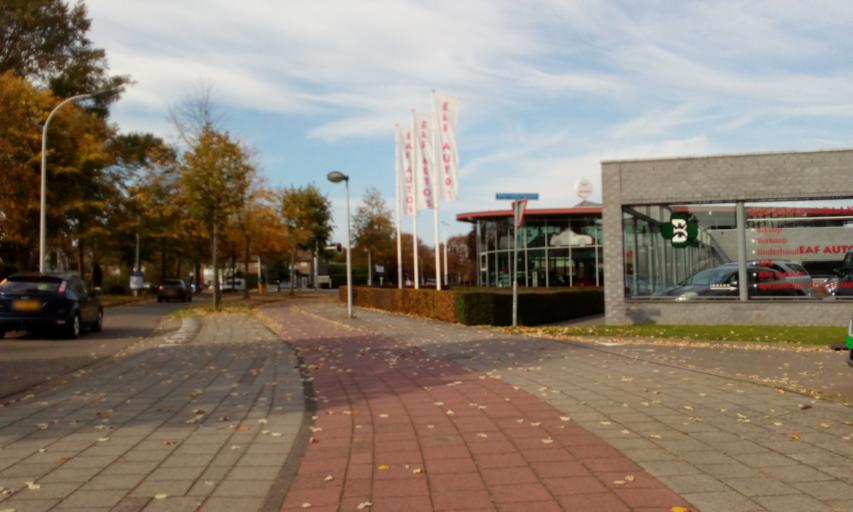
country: NL
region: South Holland
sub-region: Gemeente Voorschoten
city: Voorschoten
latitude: 52.1183
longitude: 4.4395
